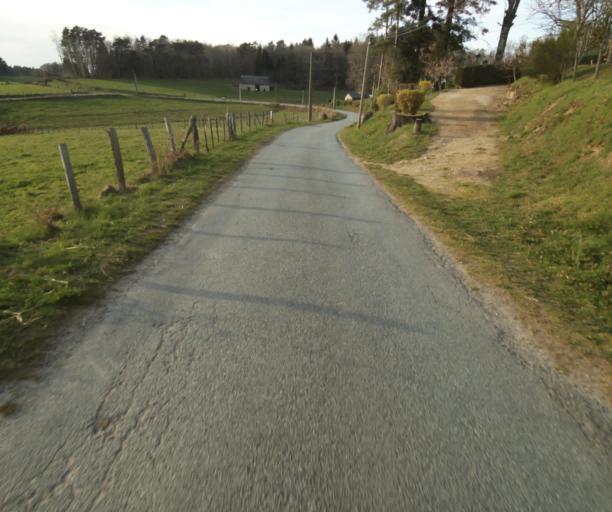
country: FR
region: Limousin
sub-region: Departement de la Correze
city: Correze
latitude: 45.3787
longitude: 1.8636
